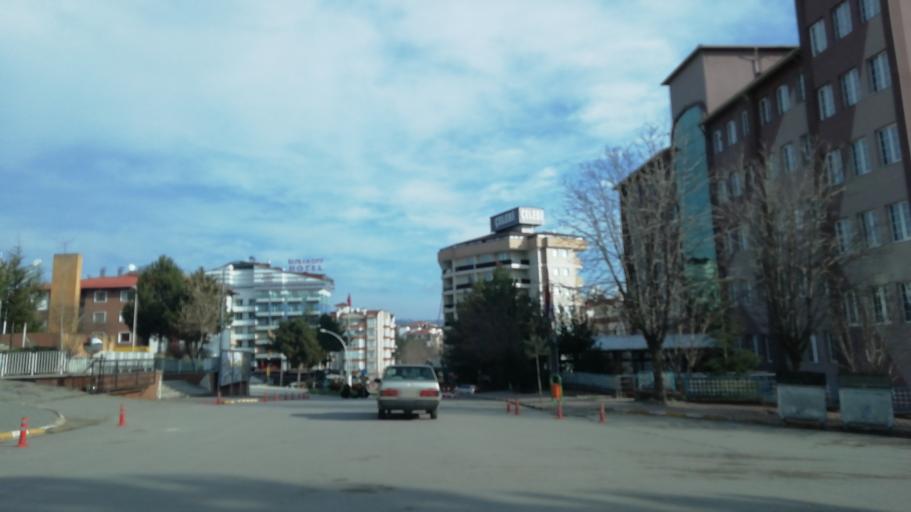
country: TR
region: Karabuk
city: Safranbolu
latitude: 41.2542
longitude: 32.6761
